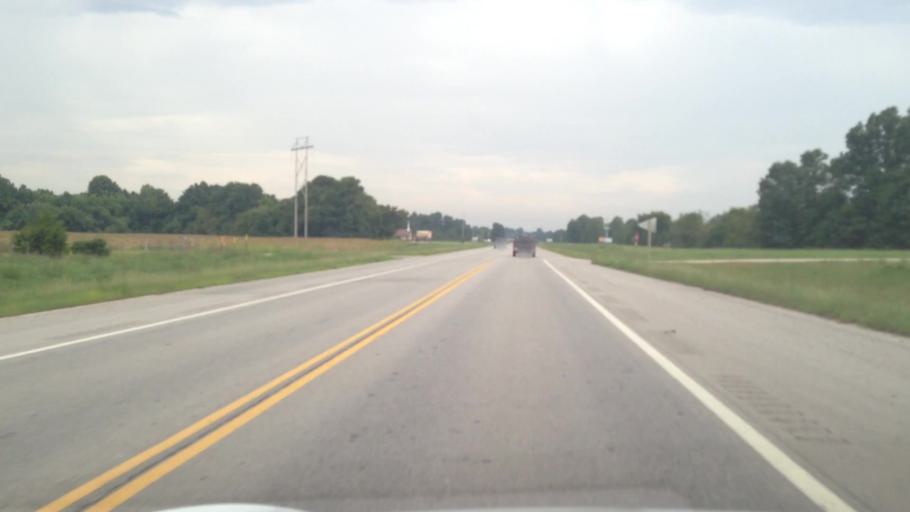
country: US
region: Kansas
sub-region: Cherokee County
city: Baxter Springs
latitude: 37.0716
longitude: -94.7209
